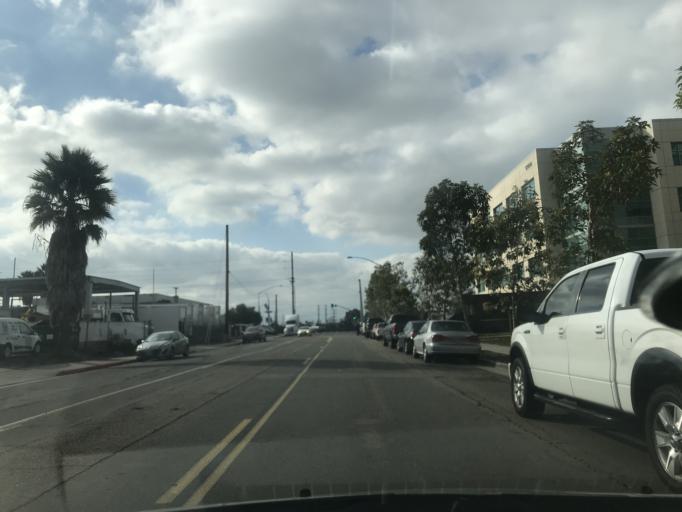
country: US
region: California
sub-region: San Diego County
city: San Diego
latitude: 32.8329
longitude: -117.1293
